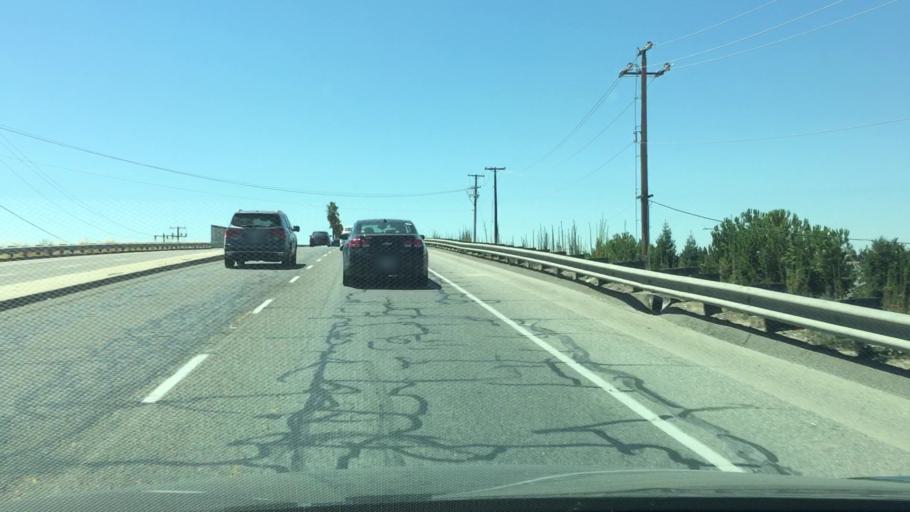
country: US
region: California
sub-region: Fresno County
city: West Park
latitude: 36.8371
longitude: -119.8841
